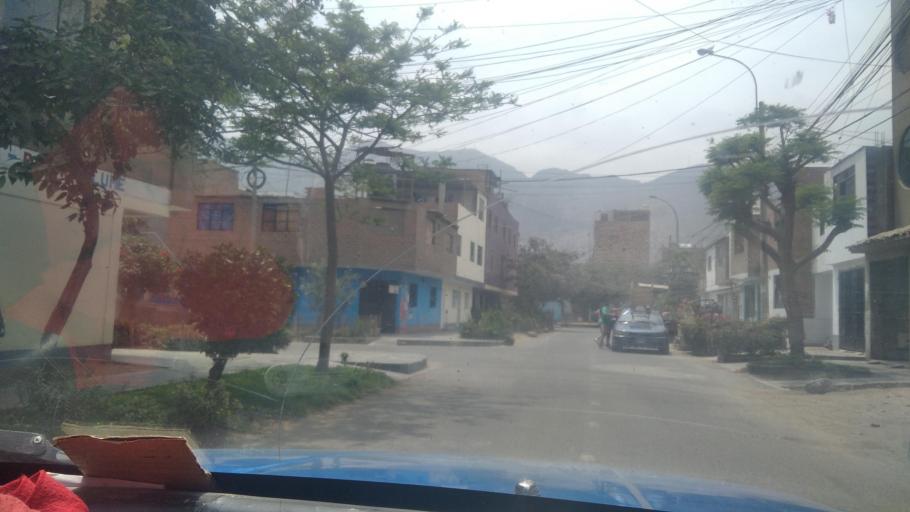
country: PE
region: Lima
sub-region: Lima
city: Independencia
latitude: -11.9860
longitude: -77.0103
